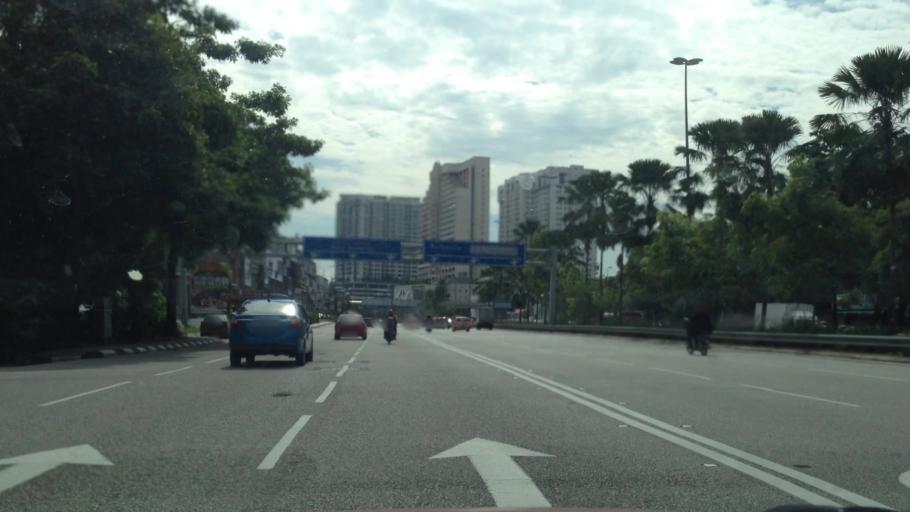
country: MY
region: Kuala Lumpur
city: Kuala Lumpur
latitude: 3.0823
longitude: 101.6684
